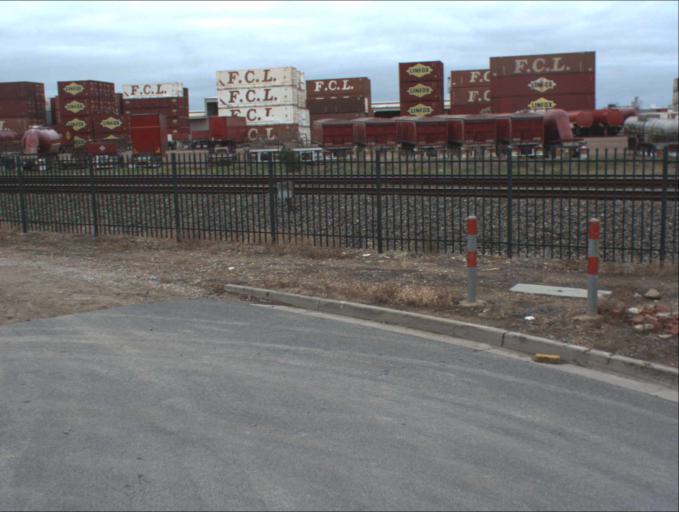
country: AU
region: South Australia
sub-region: Port Adelaide Enfield
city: Blair Athol
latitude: -34.8471
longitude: 138.5803
